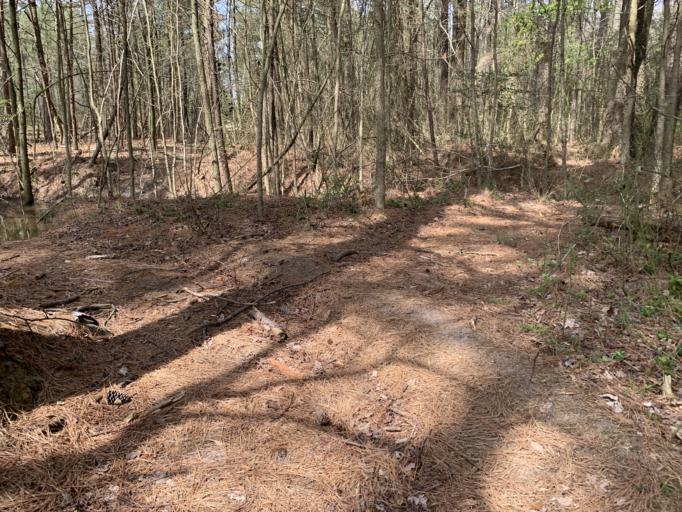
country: US
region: Delaware
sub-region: Sussex County
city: Millsboro
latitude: 38.5445
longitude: -75.3983
